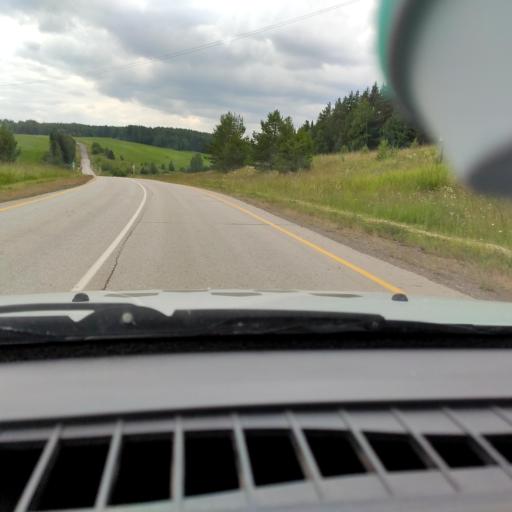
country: RU
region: Perm
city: Kukushtan
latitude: 57.3076
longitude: 56.5404
